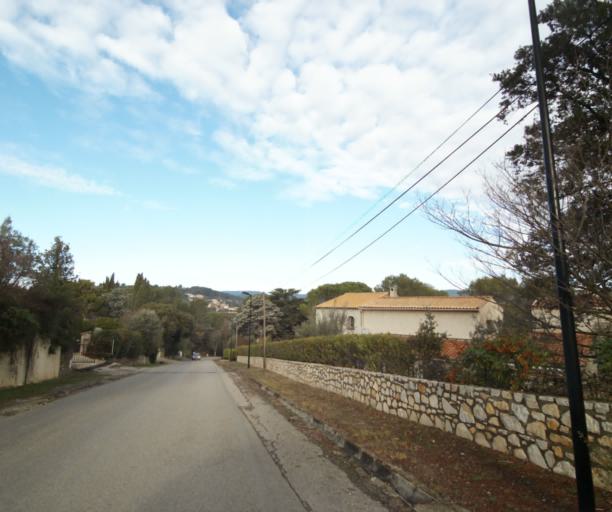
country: FR
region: Provence-Alpes-Cote d'Azur
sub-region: Departement du Var
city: Trans-en-Provence
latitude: 43.4904
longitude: 6.4949
